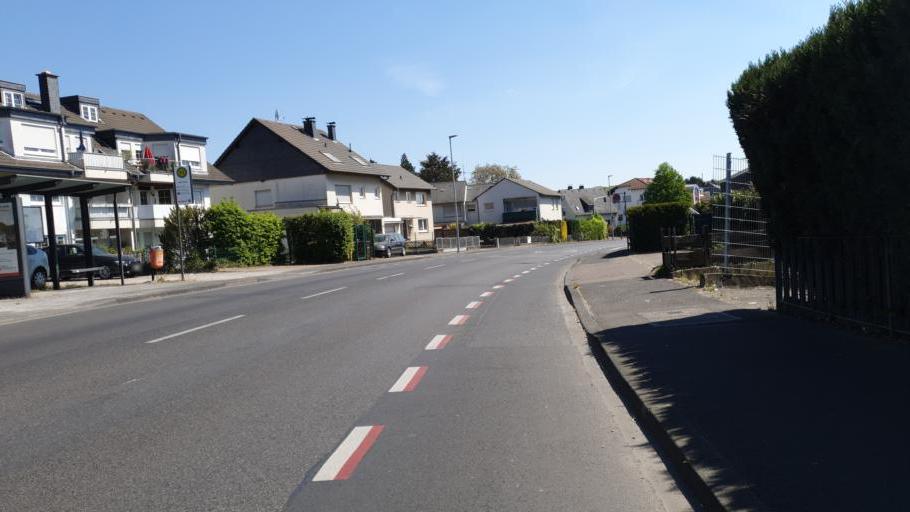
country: DE
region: North Rhine-Westphalia
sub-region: Regierungsbezirk Koln
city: Odenthal
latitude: 51.0037
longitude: 7.0952
